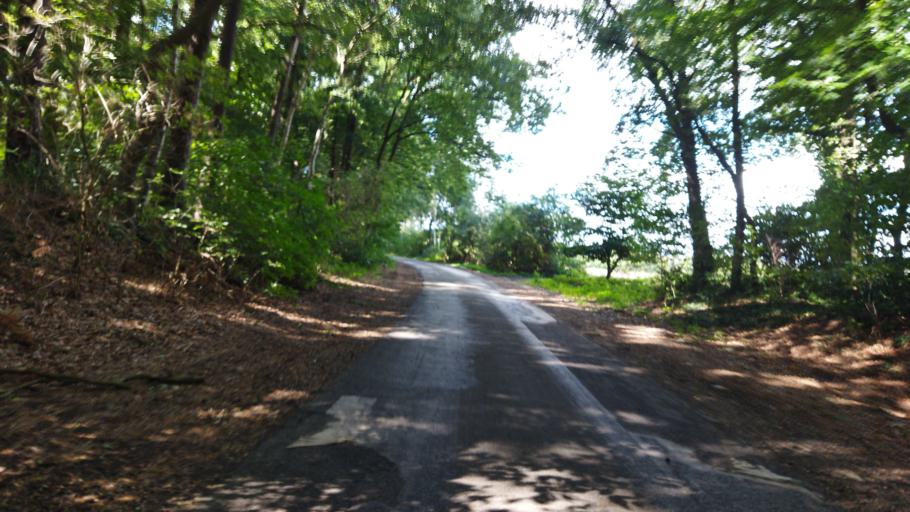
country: DE
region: Lower Saxony
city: Lingen
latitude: 52.4581
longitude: 7.3563
